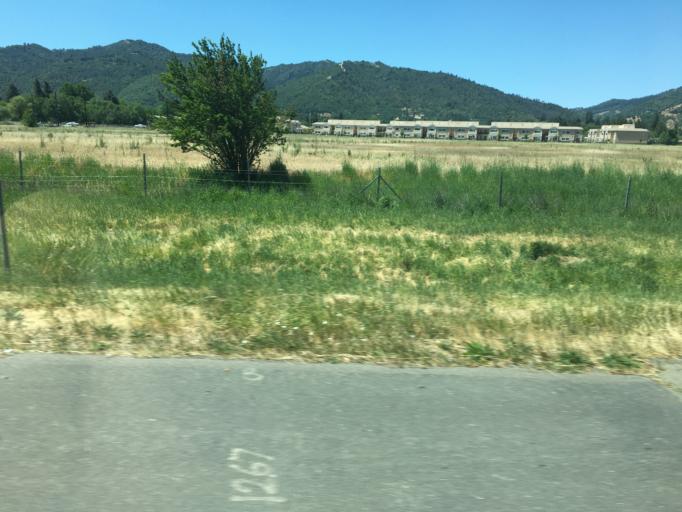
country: US
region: California
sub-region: Mendocino County
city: Ukiah
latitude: 39.1608
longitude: -123.1988
